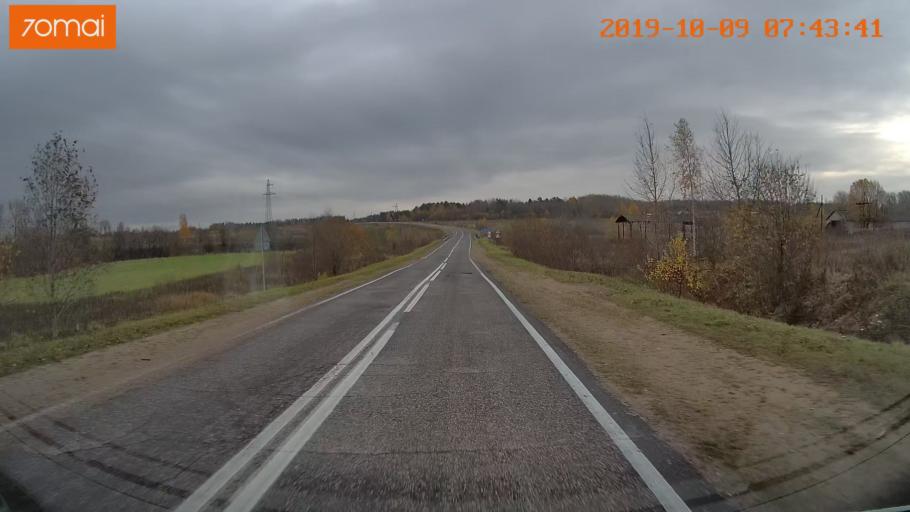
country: RU
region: Jaroslavl
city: Kukoboy
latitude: 58.6456
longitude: 39.7392
